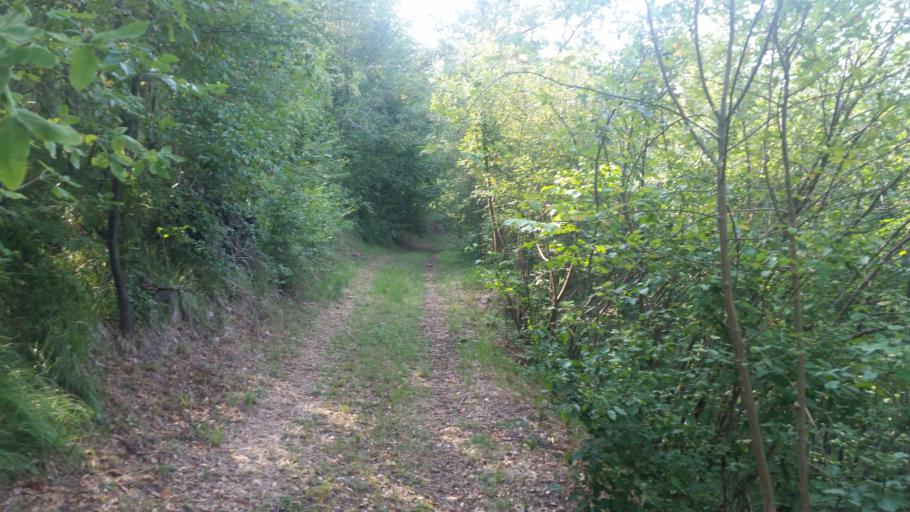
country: IT
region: Lombardy
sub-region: Provincia di Pavia
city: Menconico
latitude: 44.8259
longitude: 9.2548
